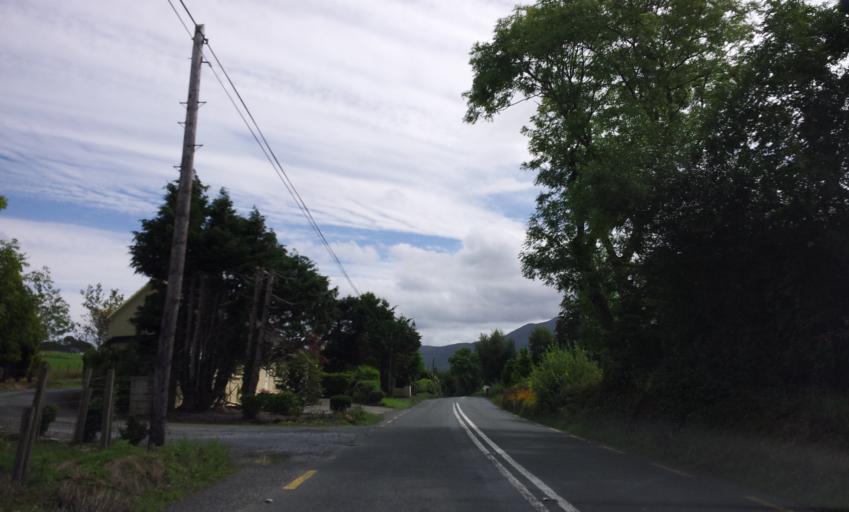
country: IE
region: Munster
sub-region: Ciarrai
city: Killorglin
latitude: 52.0797
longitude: -9.6609
